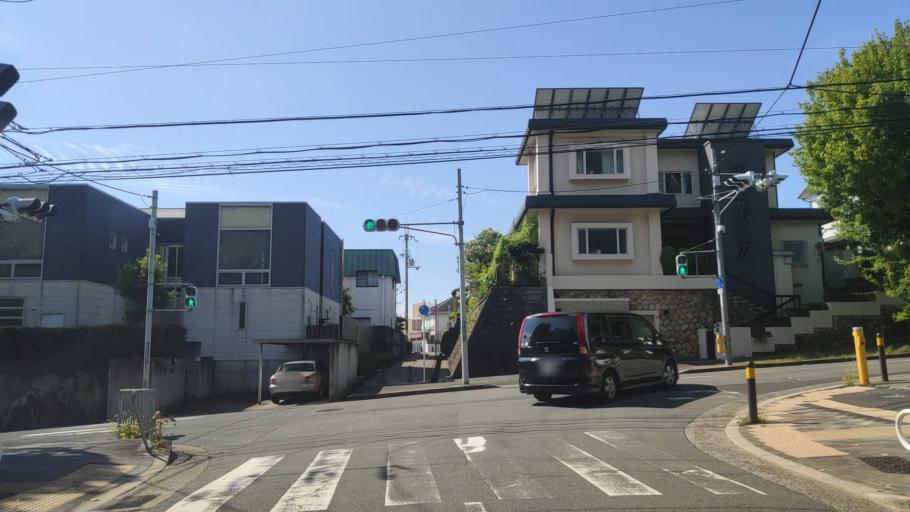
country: JP
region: Osaka
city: Mino
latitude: 34.8248
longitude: 135.5139
